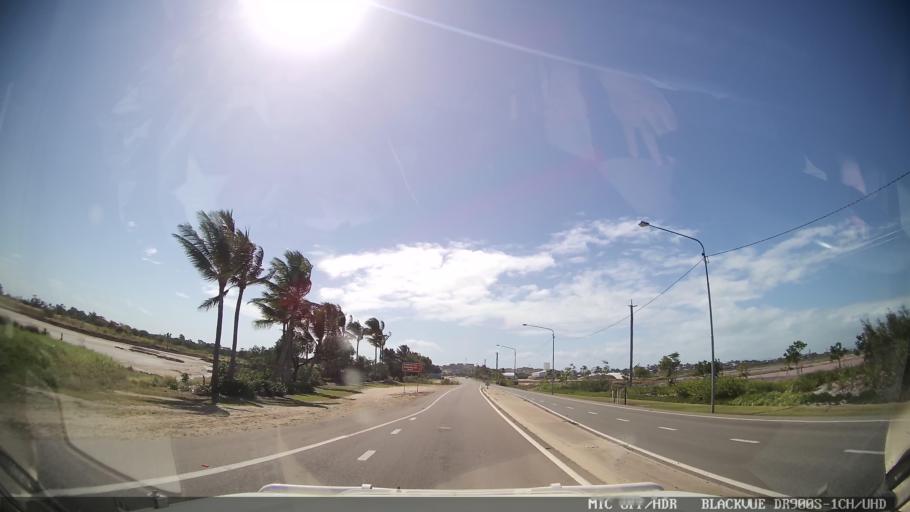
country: AU
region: Queensland
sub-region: Whitsunday
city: Bowen
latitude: -20.0148
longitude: 148.2219
